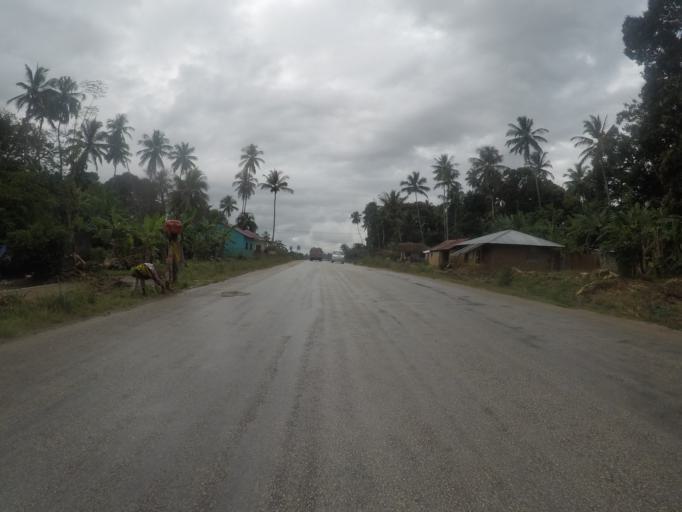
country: TZ
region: Zanzibar Central/South
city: Koani
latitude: -6.0297
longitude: 39.2377
